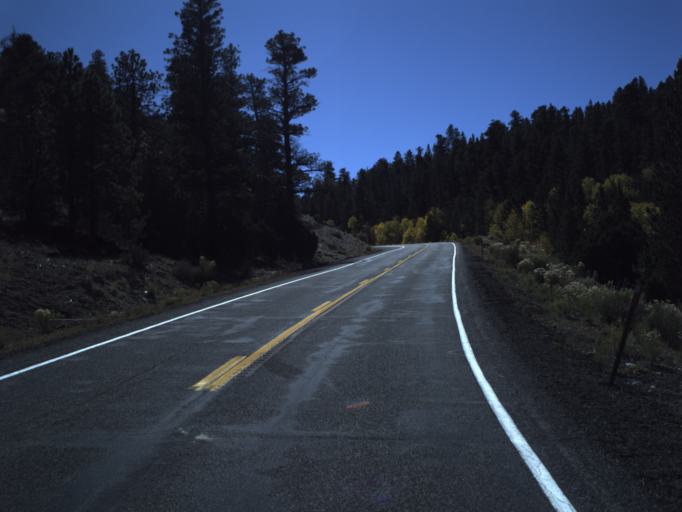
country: US
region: Utah
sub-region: Wayne County
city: Loa
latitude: 38.1751
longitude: -111.3455
